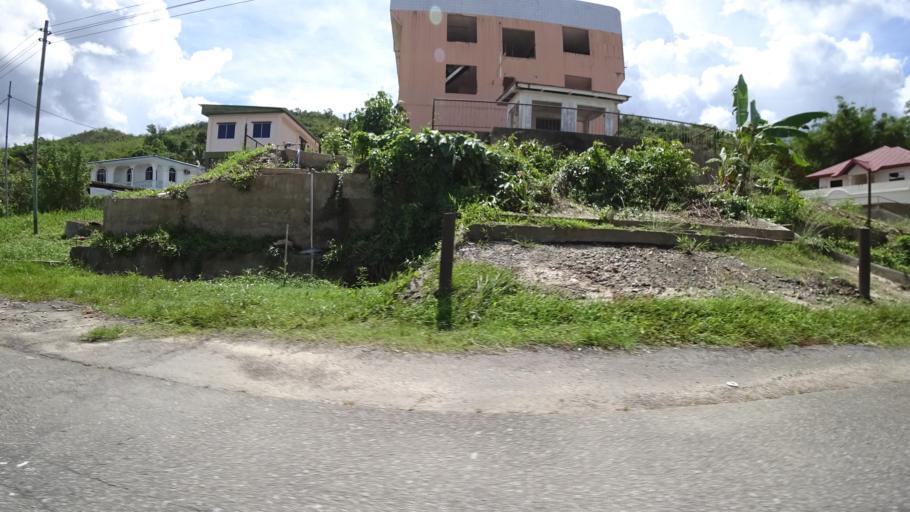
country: BN
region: Brunei and Muara
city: Bandar Seri Begawan
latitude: 4.8883
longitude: 114.9745
